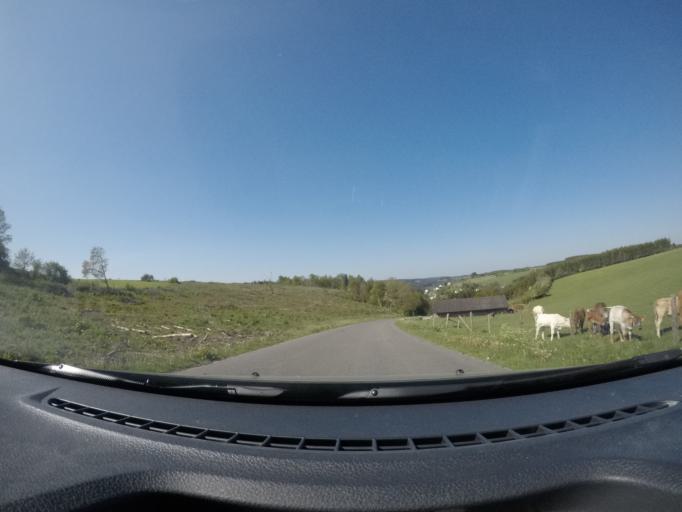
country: BE
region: Wallonia
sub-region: Province du Luxembourg
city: Martelange
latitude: 49.8574
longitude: 5.7061
